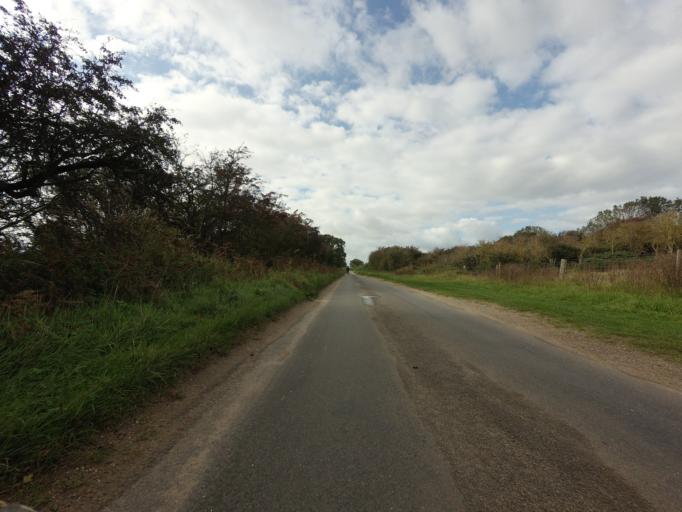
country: GB
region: England
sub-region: Norfolk
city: Hunstanton
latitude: 52.9339
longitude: 0.5620
